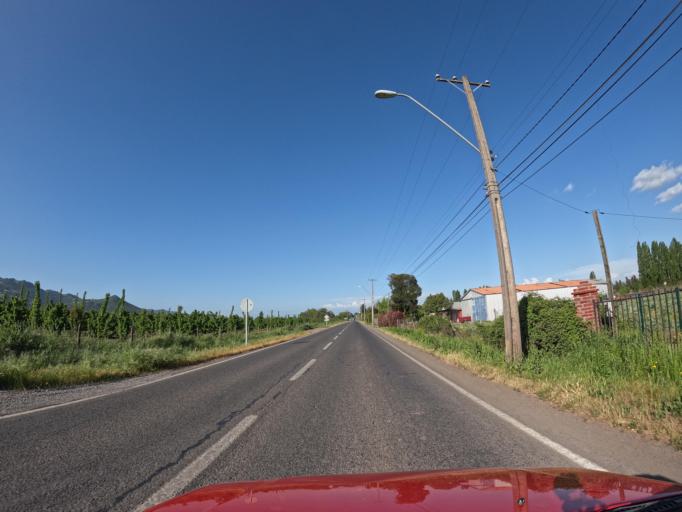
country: CL
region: Maule
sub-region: Provincia de Curico
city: Teno
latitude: -34.8718
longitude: -71.2227
